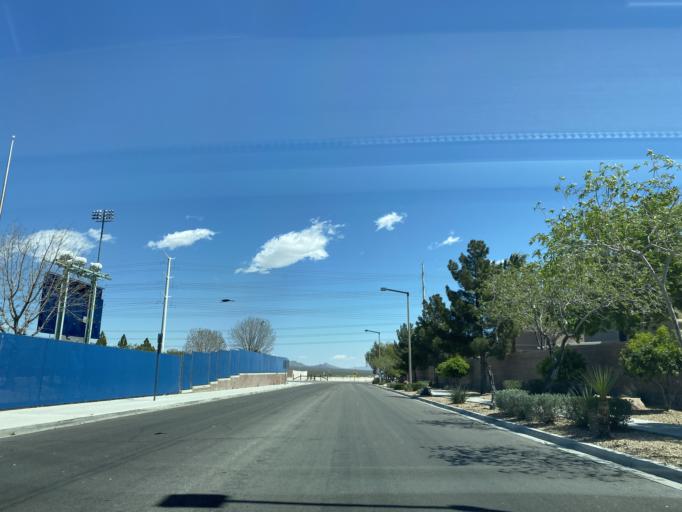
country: US
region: Nevada
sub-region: Clark County
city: North Las Vegas
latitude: 36.3170
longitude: -115.2088
